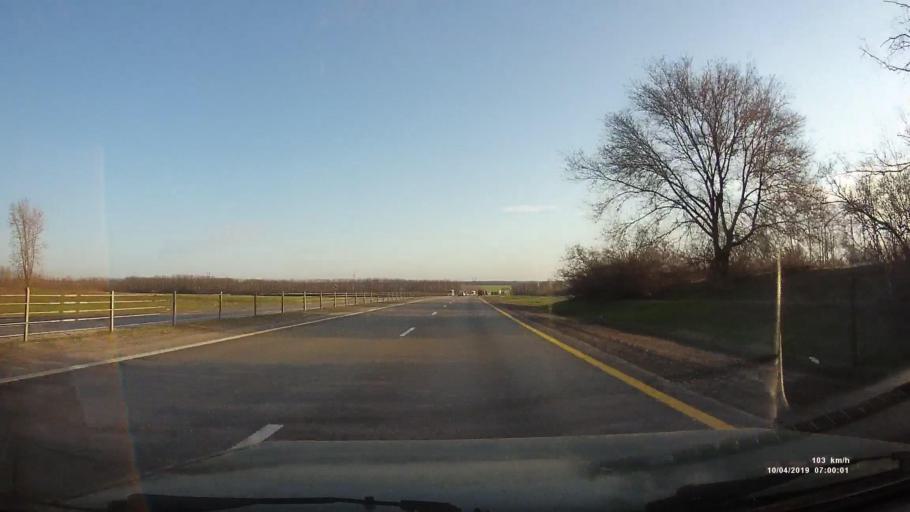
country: RU
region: Rostov
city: Grushevskaya
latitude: 47.5758
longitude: 39.9699
